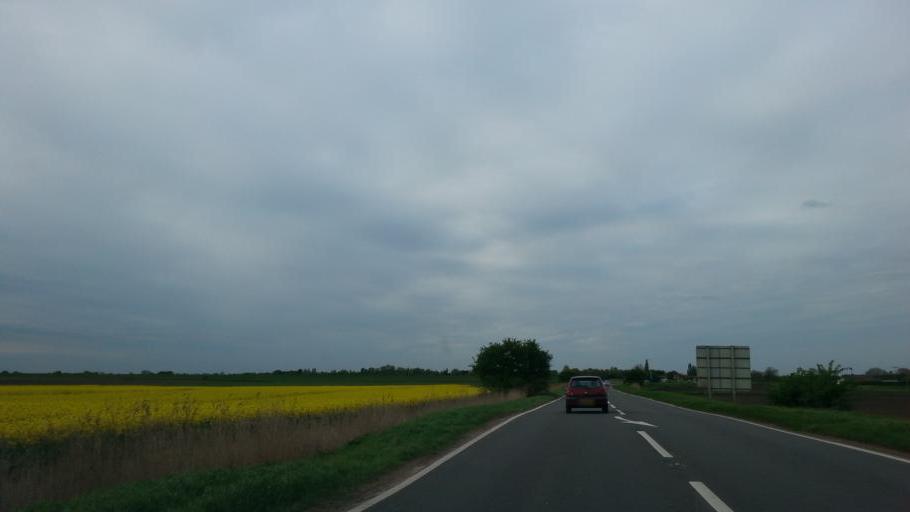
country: GB
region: England
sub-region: Cambridgeshire
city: March
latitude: 52.5944
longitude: 0.0601
